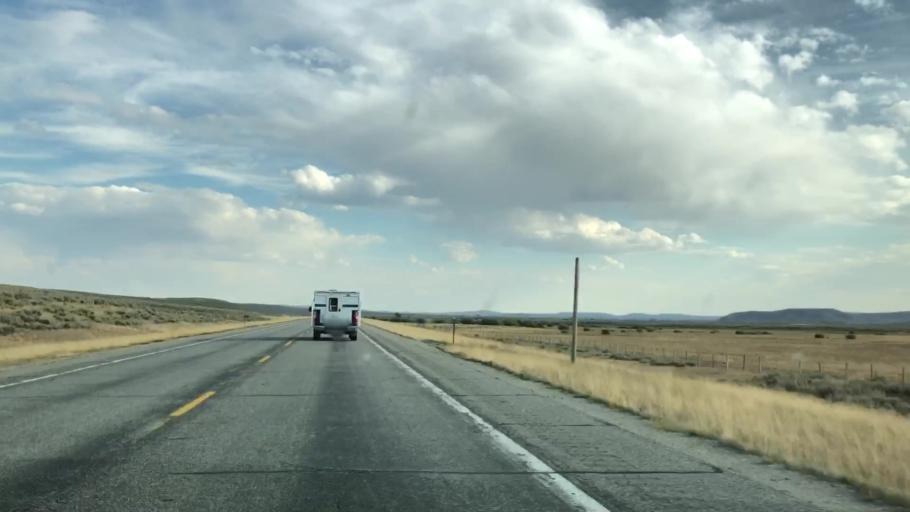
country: US
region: Wyoming
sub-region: Sublette County
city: Pinedale
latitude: 43.0289
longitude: -110.1264
